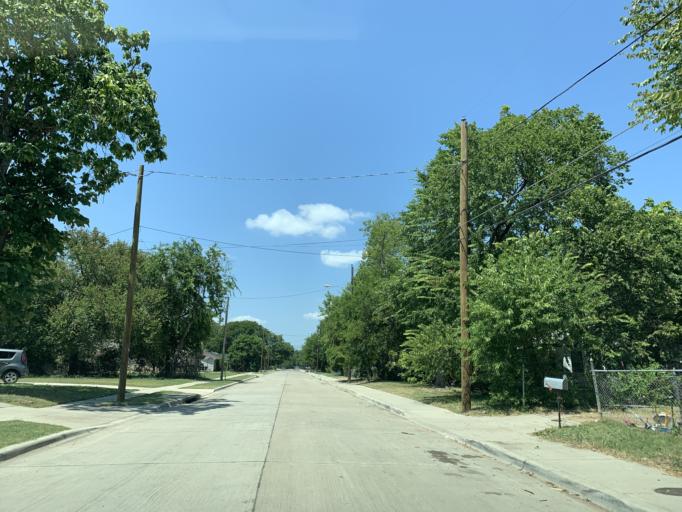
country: US
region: Texas
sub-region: Dallas County
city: Hutchins
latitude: 32.6870
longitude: -96.7742
